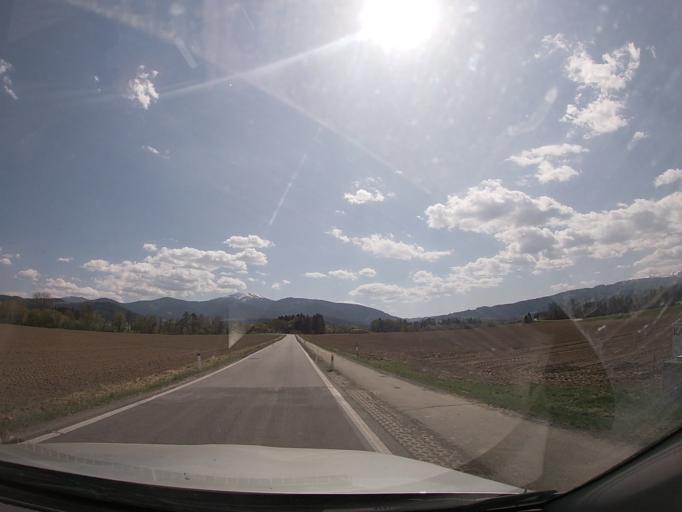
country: AT
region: Styria
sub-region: Politischer Bezirk Murtal
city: Zeltweg
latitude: 47.1794
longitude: 14.7539
